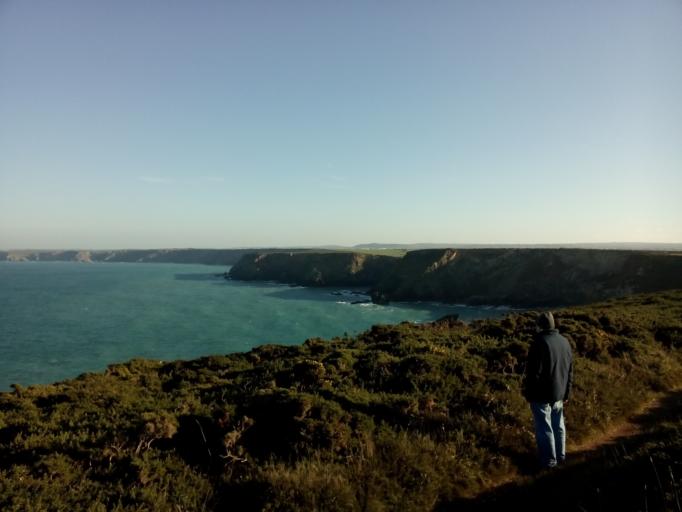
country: GB
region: England
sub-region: Cornwall
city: Hayle
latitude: 50.2398
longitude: -5.3771
